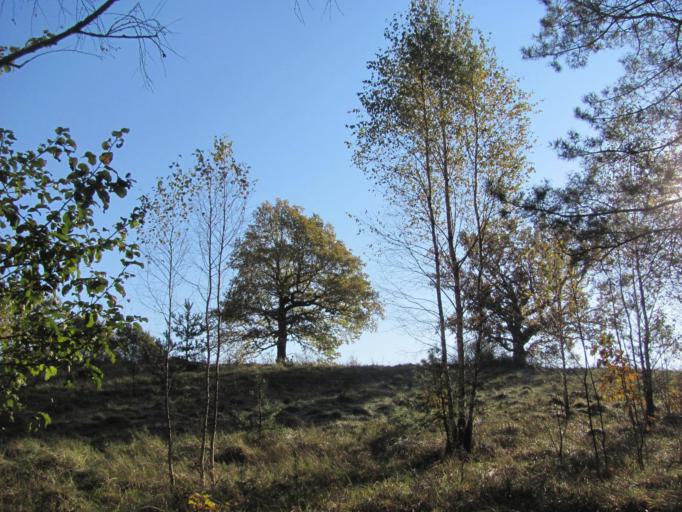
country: LT
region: Vilnius County
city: Ukmerge
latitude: 55.3623
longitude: 24.9172
